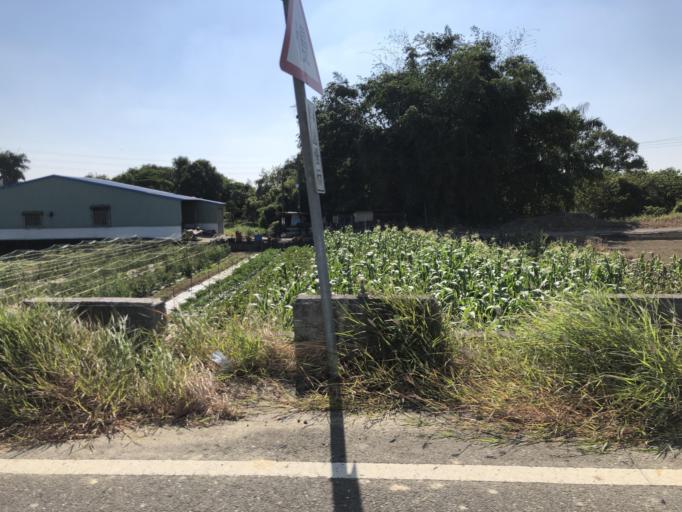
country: TW
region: Taiwan
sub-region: Tainan
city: Tainan
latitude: 23.0385
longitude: 120.3313
